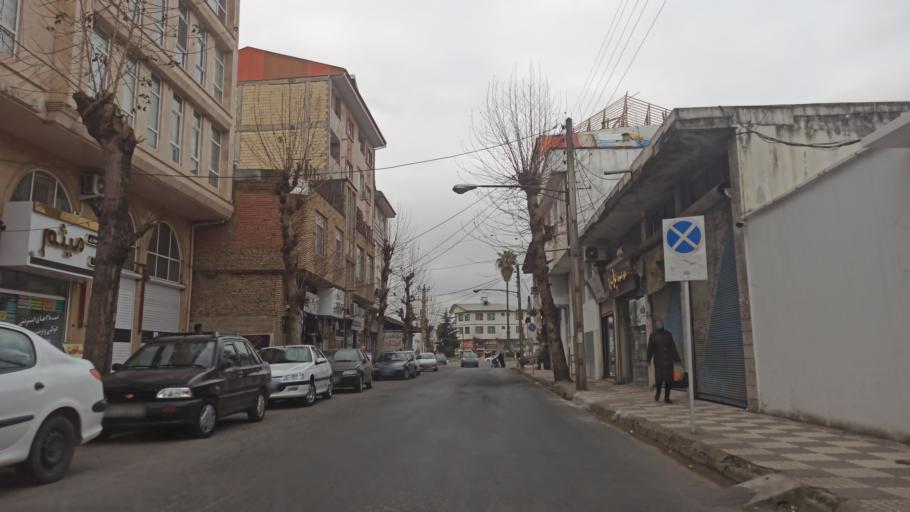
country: IR
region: Gilan
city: Fuman
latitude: 37.2300
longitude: 49.3158
